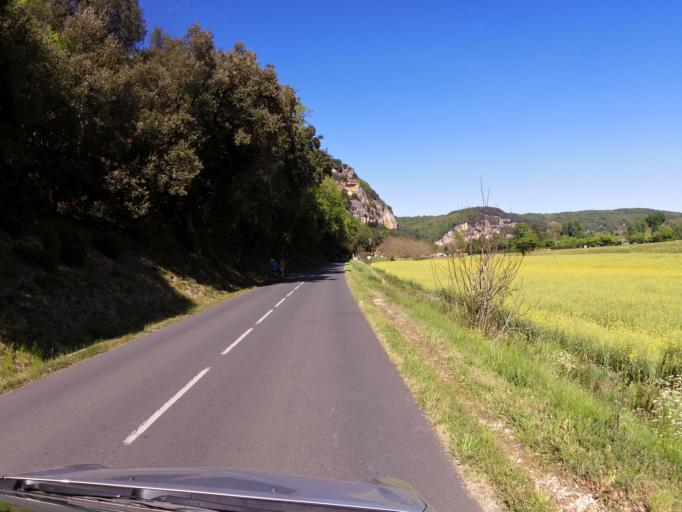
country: FR
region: Aquitaine
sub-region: Departement de la Dordogne
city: Cenac-et-Saint-Julien
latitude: 44.8229
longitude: 1.1653
